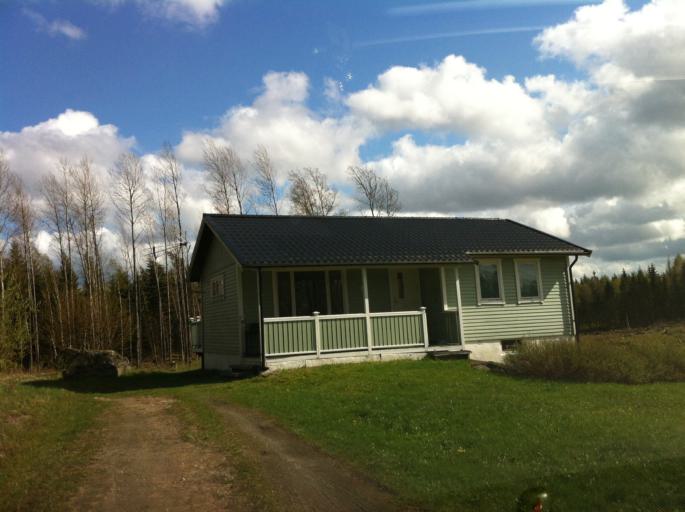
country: SE
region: Vaestra Goetaland
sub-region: Bollebygds Kommun
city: Bollebygd
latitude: 57.7643
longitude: 12.5890
